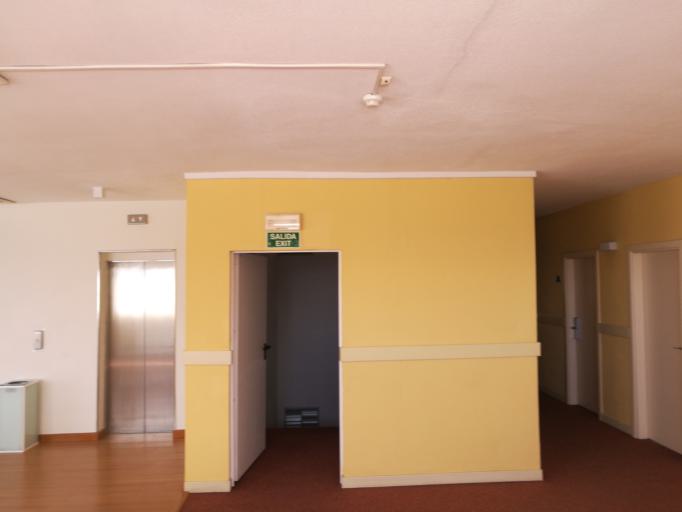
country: ES
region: Canary Islands
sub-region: Provincia de Santa Cruz de Tenerife
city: Playa de las Americas
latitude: 28.0766
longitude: -16.7308
